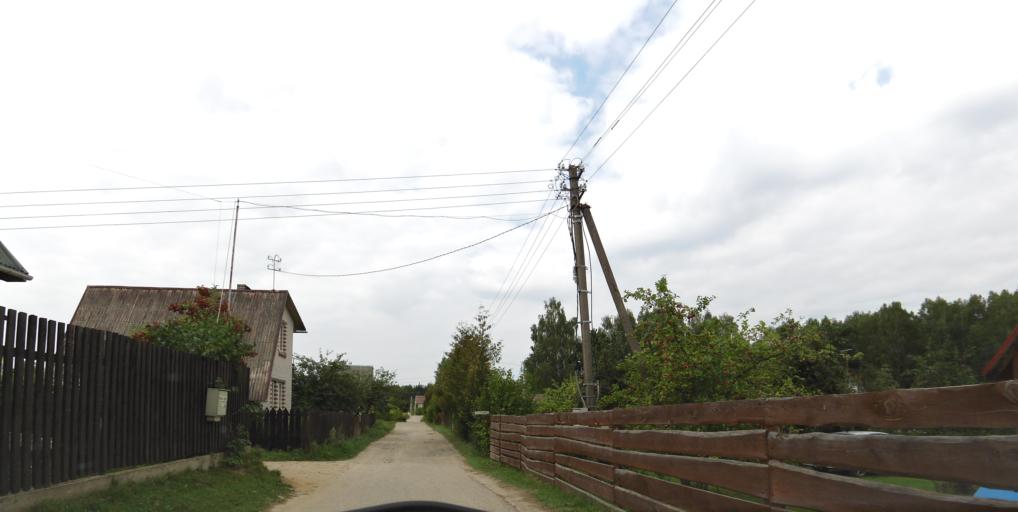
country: LT
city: Grigiskes
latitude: 54.7563
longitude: 25.0138
